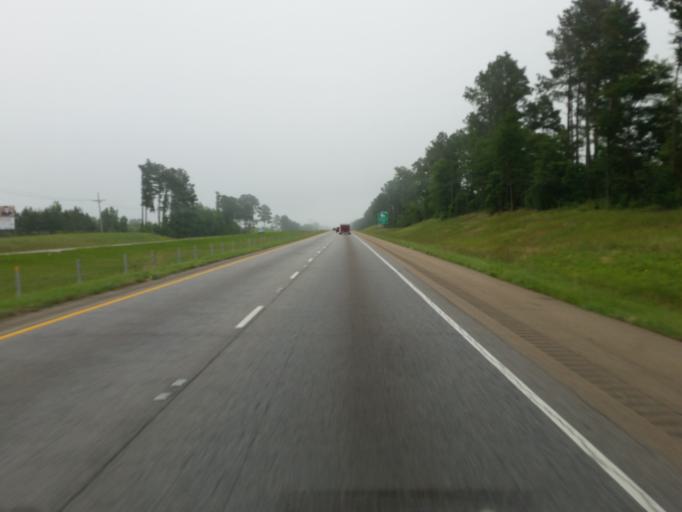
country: US
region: Louisiana
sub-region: Webster Parish
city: Minden
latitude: 32.5849
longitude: -93.2699
